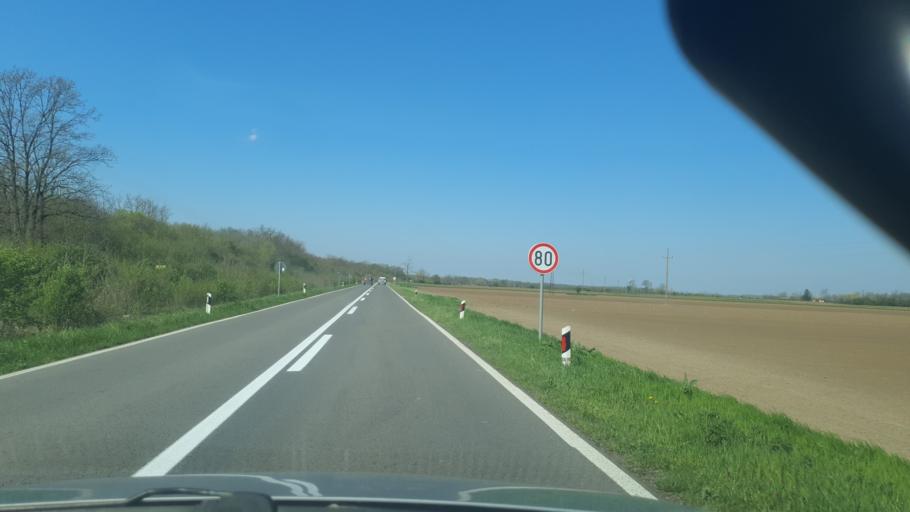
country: RS
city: Kolut
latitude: 45.8408
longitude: 18.9883
